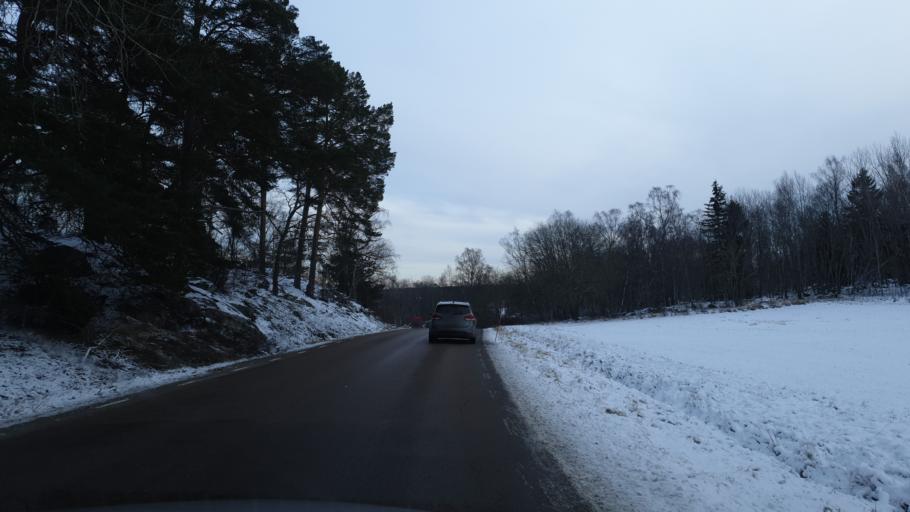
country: SE
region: Stockholm
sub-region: Sigtuna Kommun
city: Sigtuna
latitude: 59.7052
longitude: 17.6099
